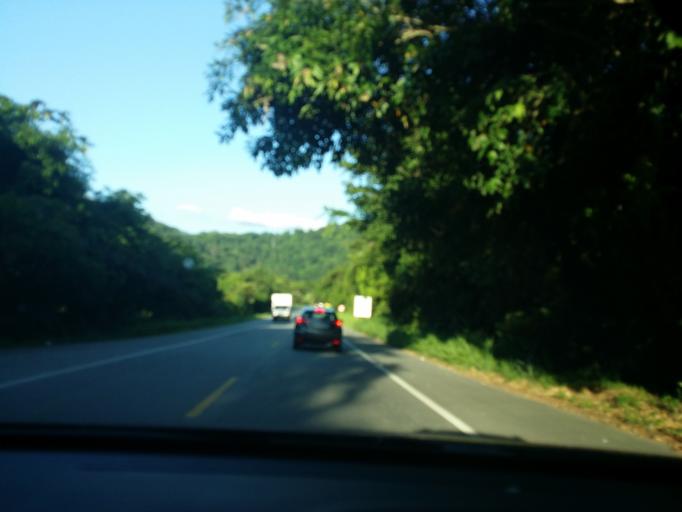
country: BR
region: Sao Paulo
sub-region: Sao Sebastiao
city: Sao Sebastiao
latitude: -23.7688
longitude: -45.6984
